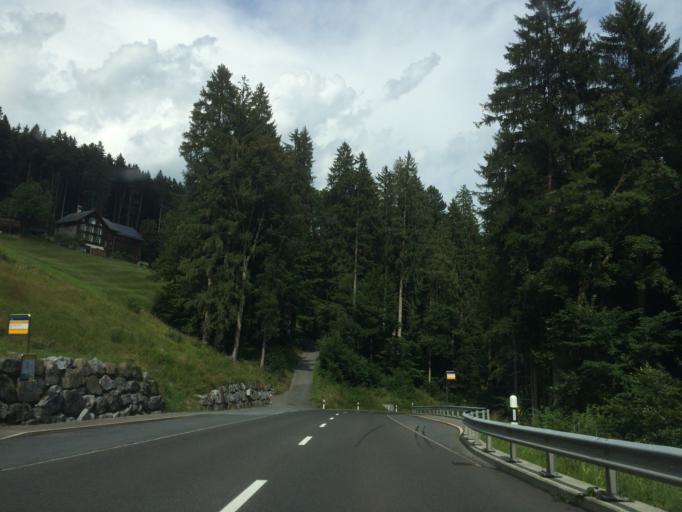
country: CH
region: Saint Gallen
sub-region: Wahlkreis Werdenberg
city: Gams
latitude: 47.1955
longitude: 9.4050
